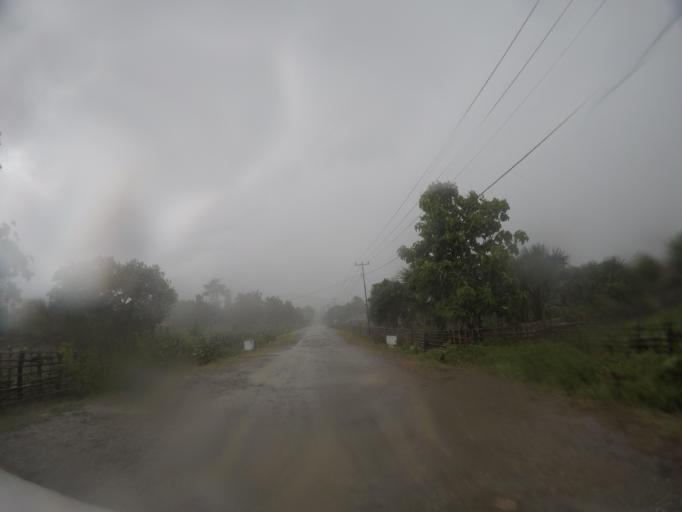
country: TL
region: Bobonaro
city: Maliana
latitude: -8.8562
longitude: 125.0964
